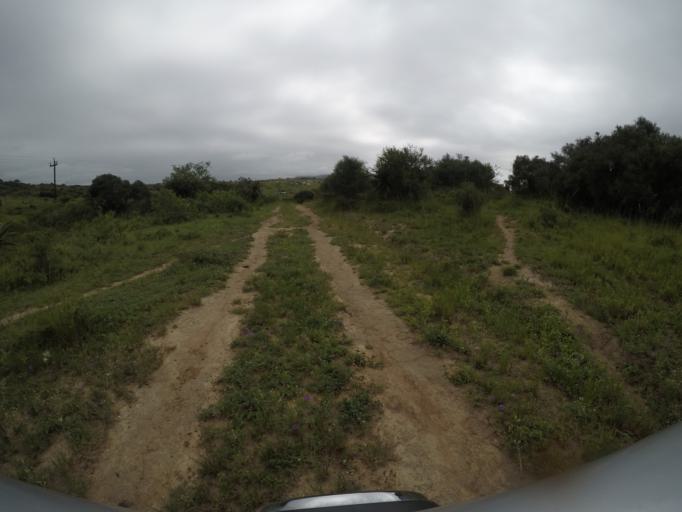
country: ZA
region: KwaZulu-Natal
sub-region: uThungulu District Municipality
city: Empangeni
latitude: -28.6075
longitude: 31.8371
